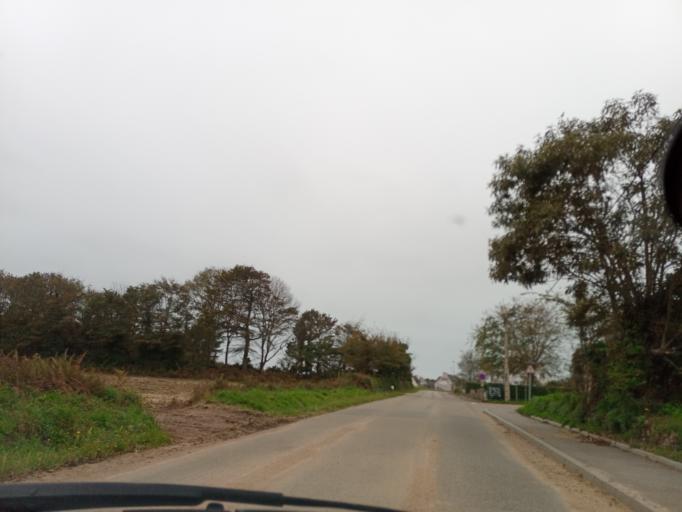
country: FR
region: Brittany
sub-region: Departement du Finistere
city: Esquibien
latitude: 48.0249
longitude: -4.5562
